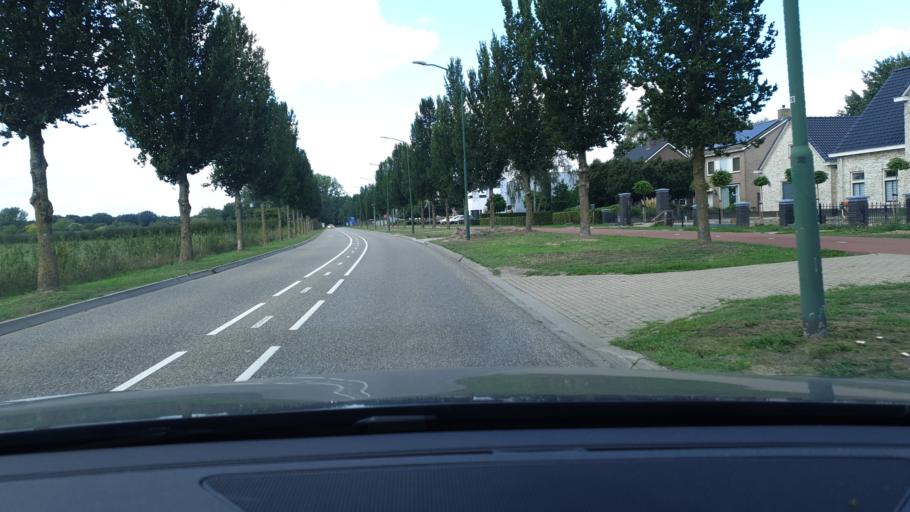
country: NL
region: North Brabant
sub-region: Gemeente Cuijk
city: Cuijk
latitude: 51.7299
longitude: 5.8639
